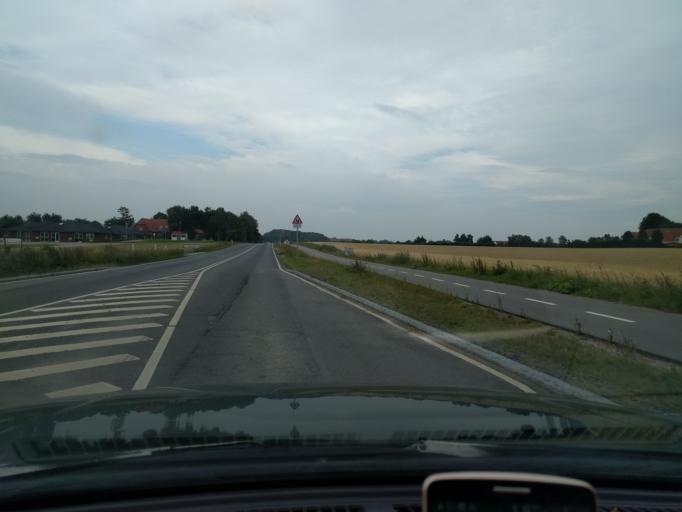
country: DK
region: Zealand
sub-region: Slagelse Kommune
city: Skaelskor
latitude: 55.3121
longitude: 11.2283
